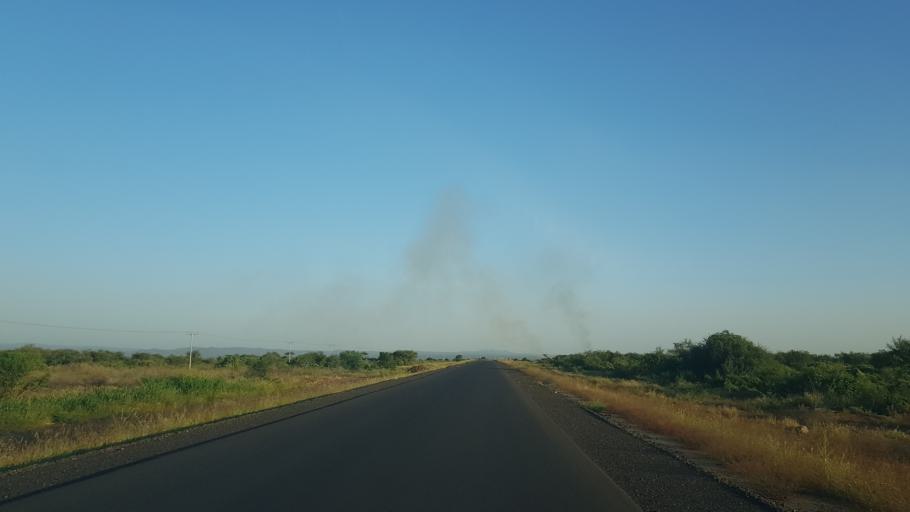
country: ET
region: Southern Nations, Nationalities, and People's Region
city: Lobuni
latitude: 5.1515
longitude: 36.1045
